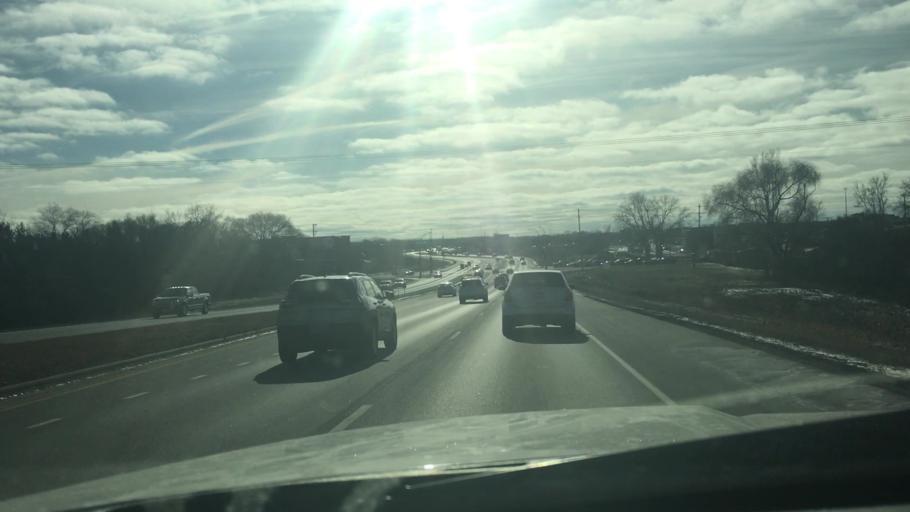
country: US
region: Minnesota
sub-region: Stearns County
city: Waite Park
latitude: 45.5610
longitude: -94.2061
